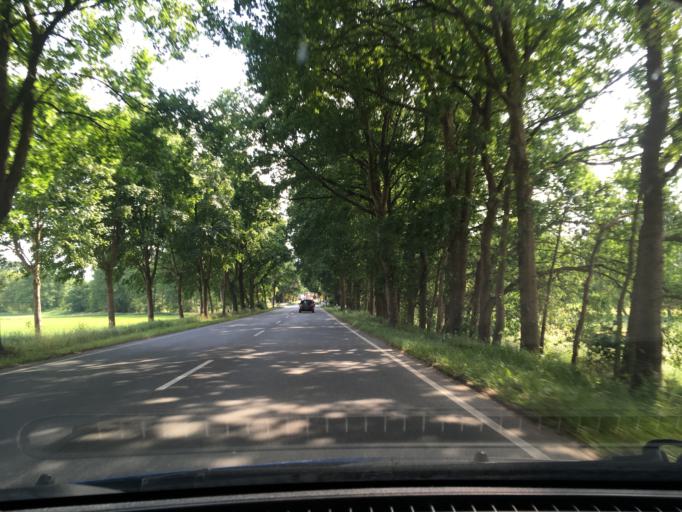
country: DE
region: Lower Saxony
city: Welle
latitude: 53.2441
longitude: 9.8045
